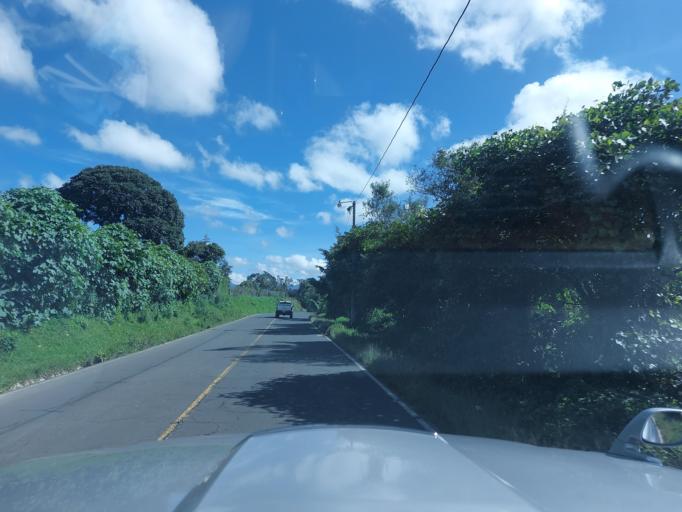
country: GT
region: Chimaltenango
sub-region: Municipio de Zaragoza
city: Zaragoza
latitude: 14.6577
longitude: -90.8971
